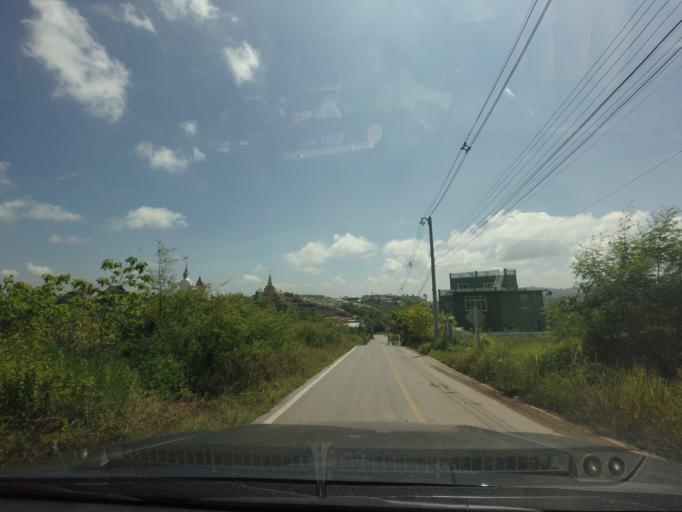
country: TH
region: Phetchabun
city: Khao Kho
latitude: 16.7911
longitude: 101.0468
